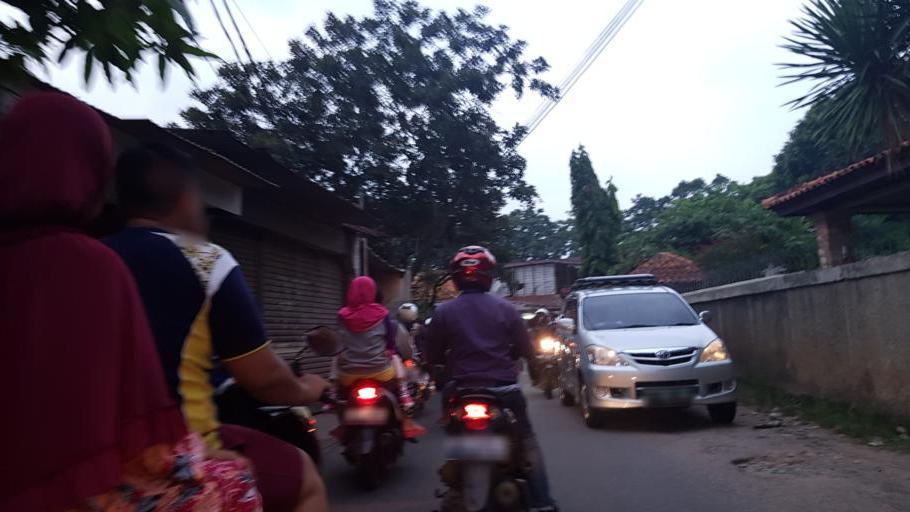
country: ID
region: West Java
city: Depok
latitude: -6.3649
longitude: 106.7982
